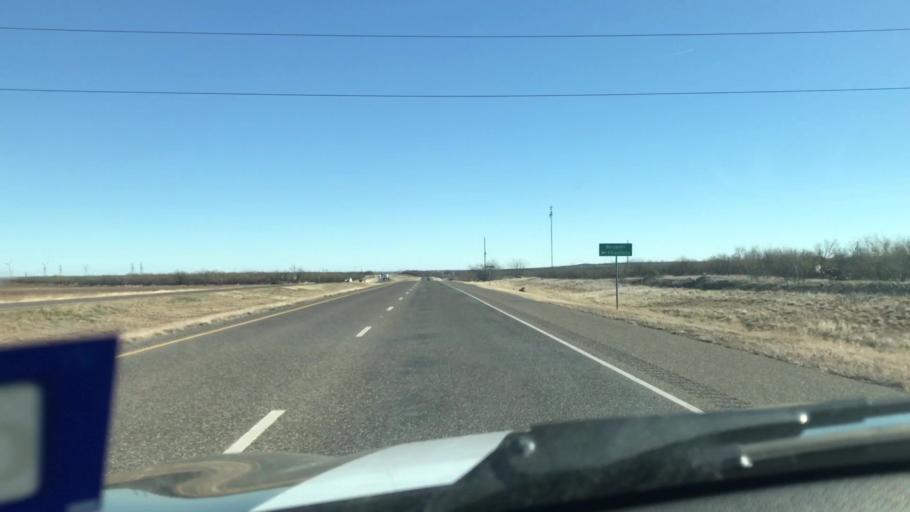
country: US
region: Texas
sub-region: Scurry County
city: Snyder
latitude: 32.8653
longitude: -101.0311
